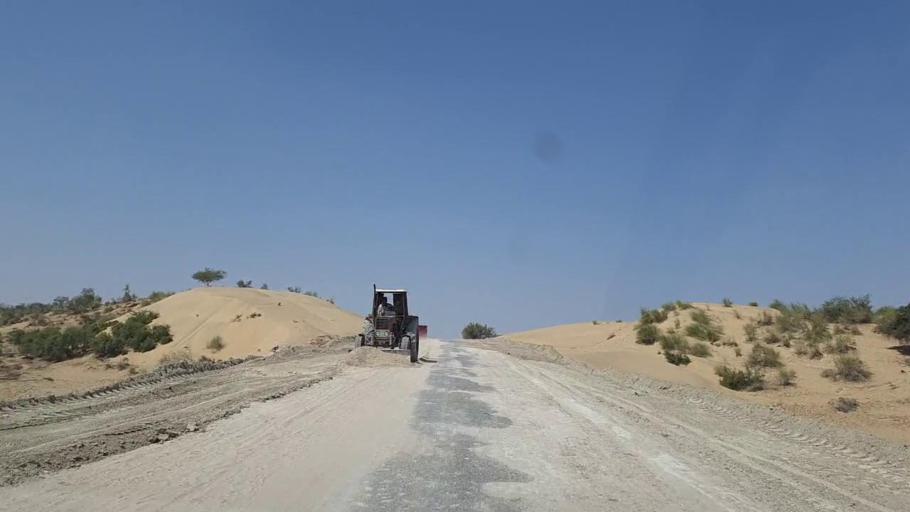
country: PK
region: Sindh
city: Diplo
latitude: 24.5866
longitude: 69.5583
